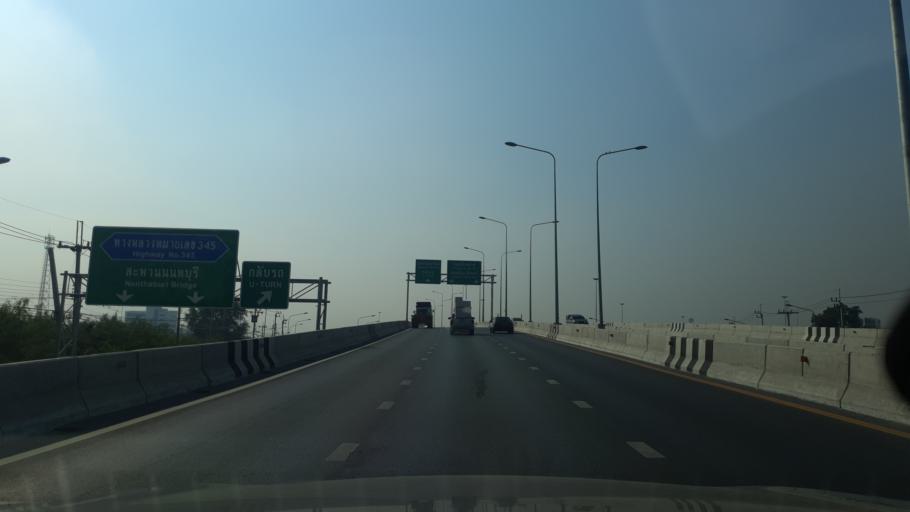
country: TH
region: Nonthaburi
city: Bang Bua Thong
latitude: 13.9549
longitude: 100.4584
